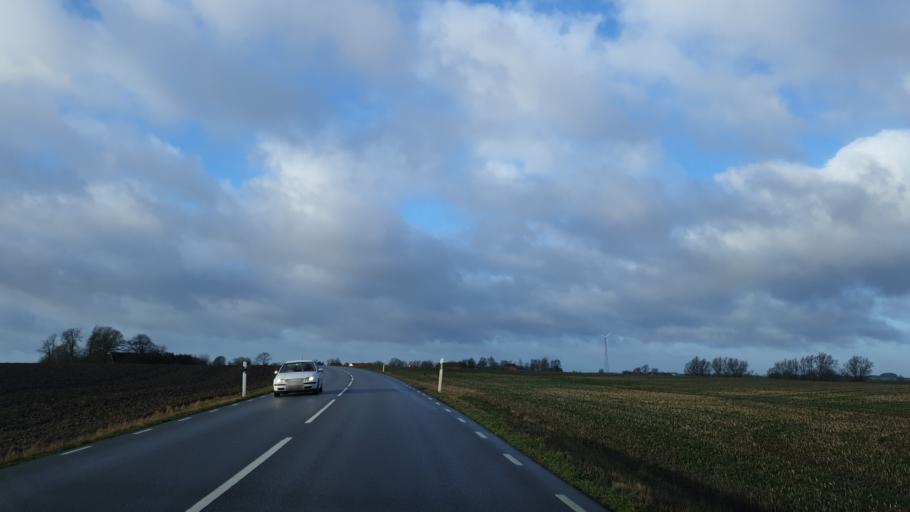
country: SE
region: Skane
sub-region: Trelleborgs Kommun
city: Anderslov
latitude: 55.4245
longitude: 13.3853
